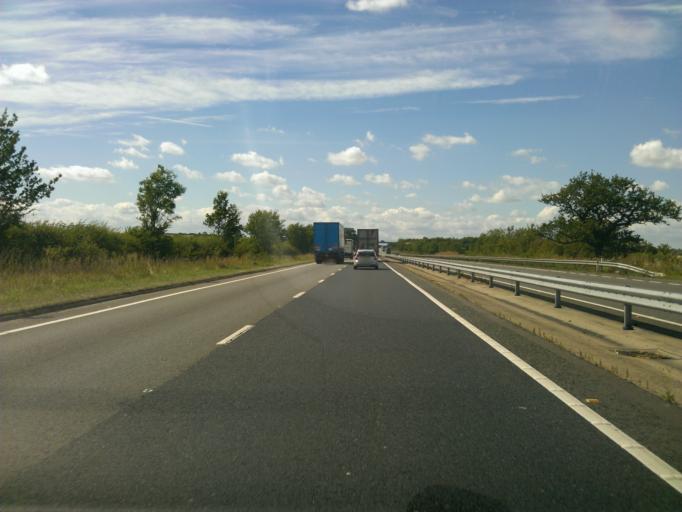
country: GB
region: England
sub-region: Bedford
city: Pertenhall
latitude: 52.3564
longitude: -0.3951
